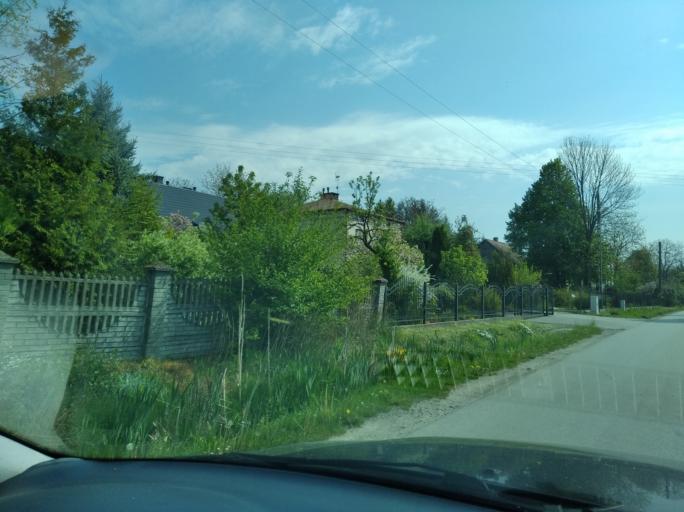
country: PL
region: Subcarpathian Voivodeship
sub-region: Powiat jaroslawski
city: Pruchnik
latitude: 49.9052
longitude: 22.5223
